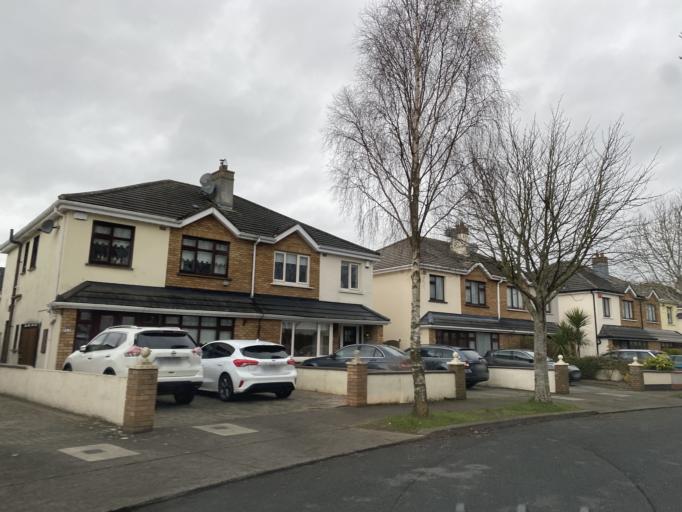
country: IE
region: Leinster
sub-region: Kildare
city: Celbridge
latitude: 53.3514
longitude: -6.5529
